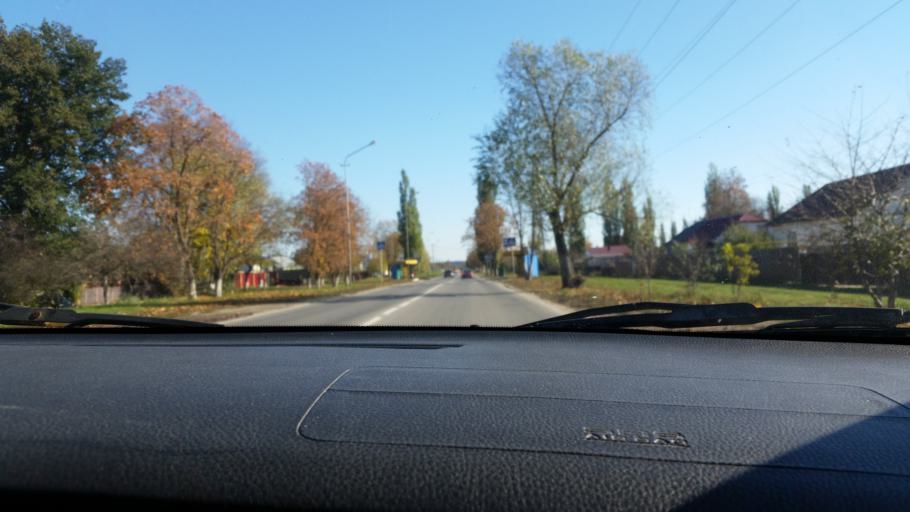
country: RU
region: Lipetsk
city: Gryazi
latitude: 52.4819
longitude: 39.9509
